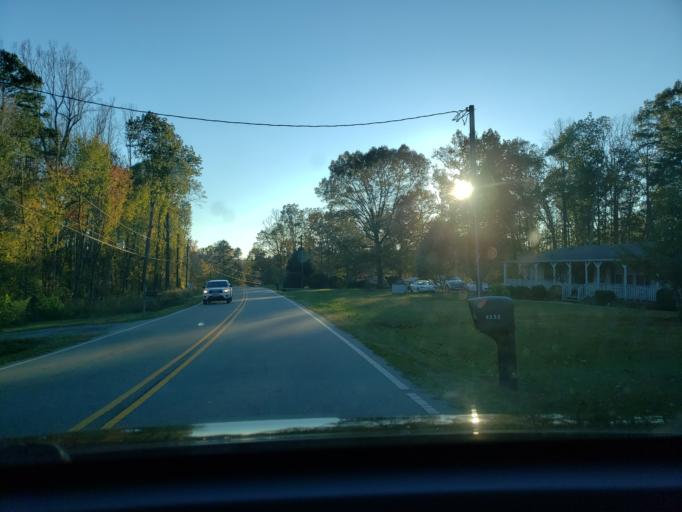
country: US
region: North Carolina
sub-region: Forsyth County
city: Walkertown
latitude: 36.2217
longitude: -80.1769
